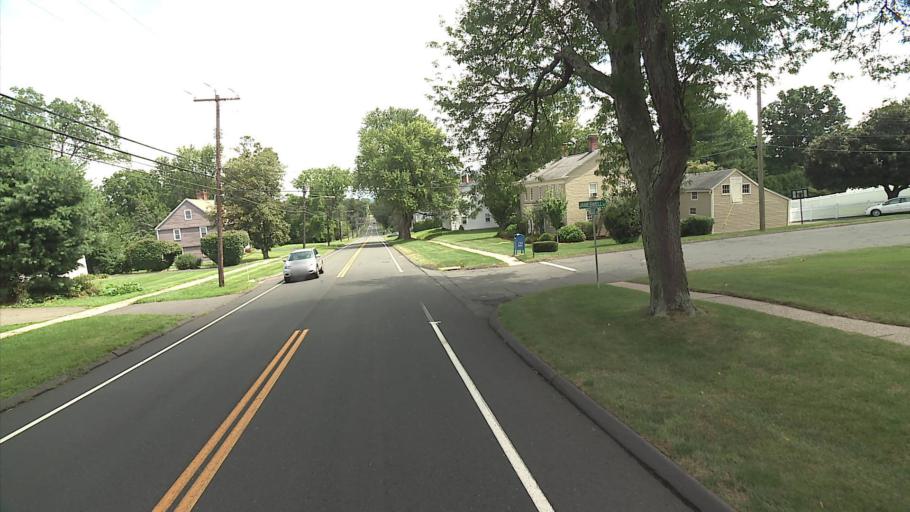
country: US
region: Connecticut
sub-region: Hartford County
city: Wethersfield
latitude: 41.7016
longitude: -72.6825
